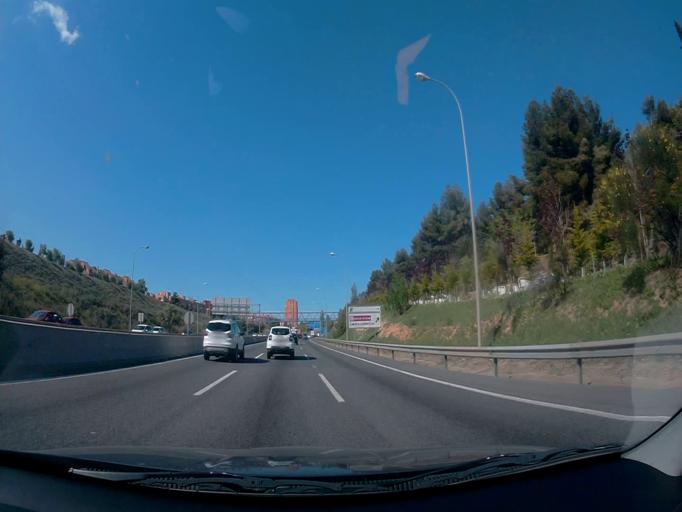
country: ES
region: Madrid
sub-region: Provincia de Madrid
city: Vicalvaro
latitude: 40.4000
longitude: -3.6264
